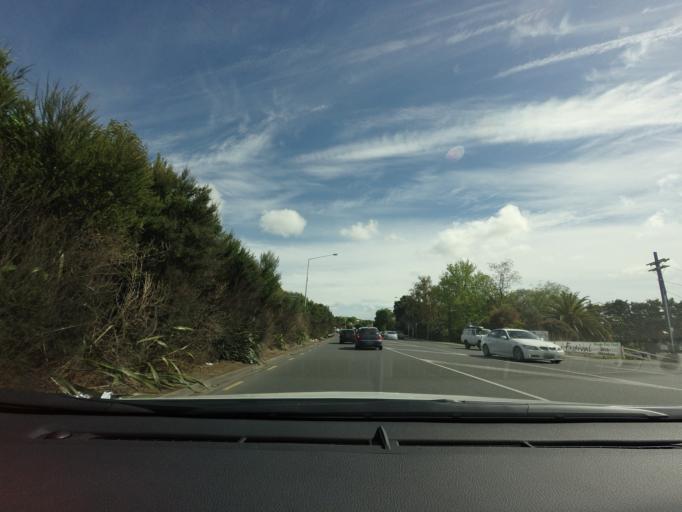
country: NZ
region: Auckland
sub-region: Auckland
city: Warkworth
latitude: -36.4033
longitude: 174.6585
